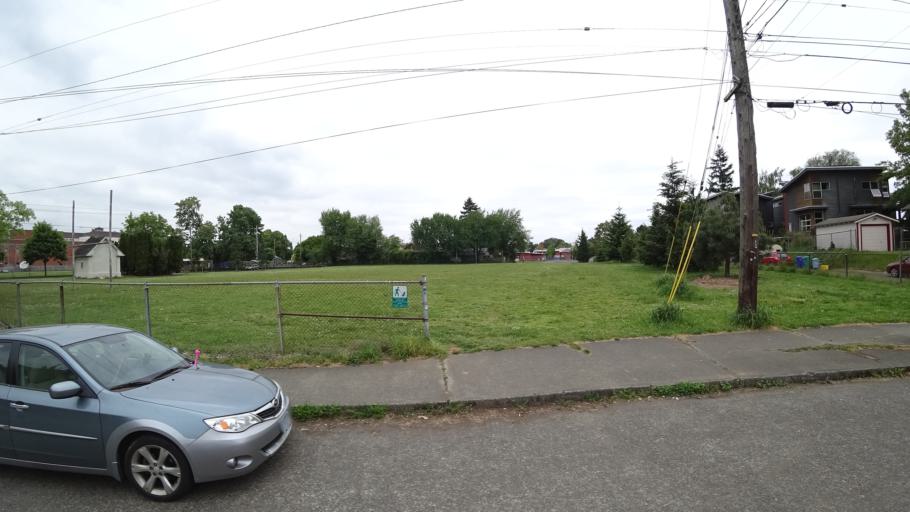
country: US
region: Oregon
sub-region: Multnomah County
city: Portland
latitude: 45.5583
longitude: -122.6729
